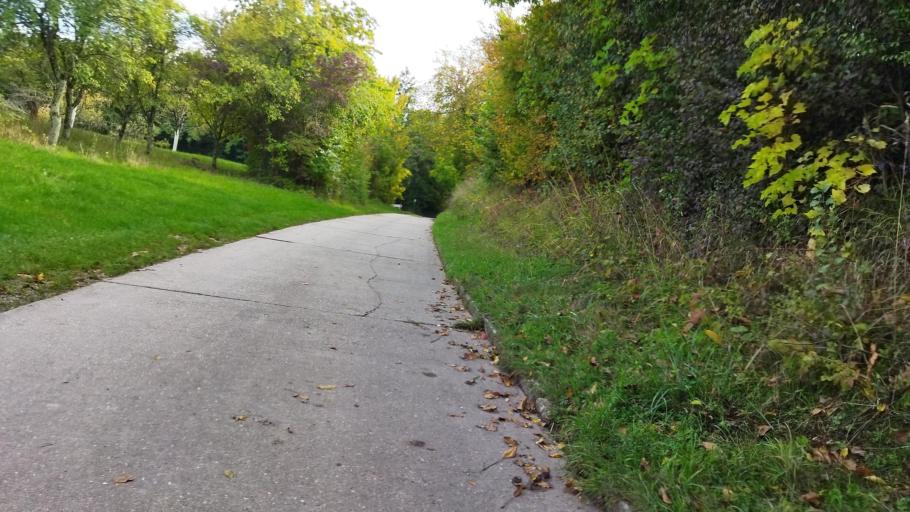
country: DE
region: Baden-Wuerttemberg
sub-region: Karlsruhe Region
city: Sulzfeld
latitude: 49.0920
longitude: 8.8658
